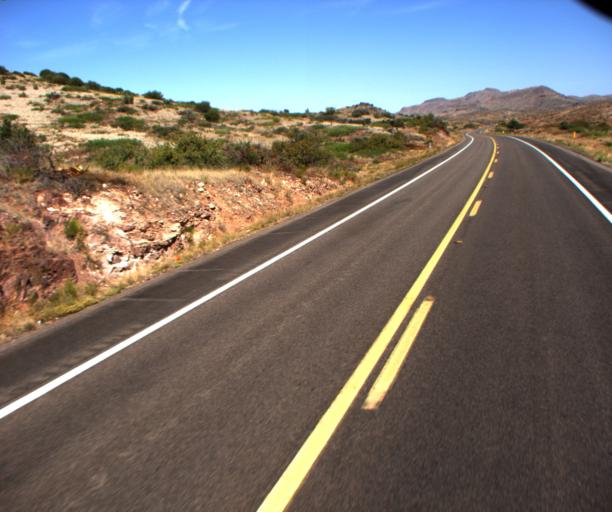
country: US
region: Arizona
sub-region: Greenlee County
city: Clifton
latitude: 32.7610
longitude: -109.2464
